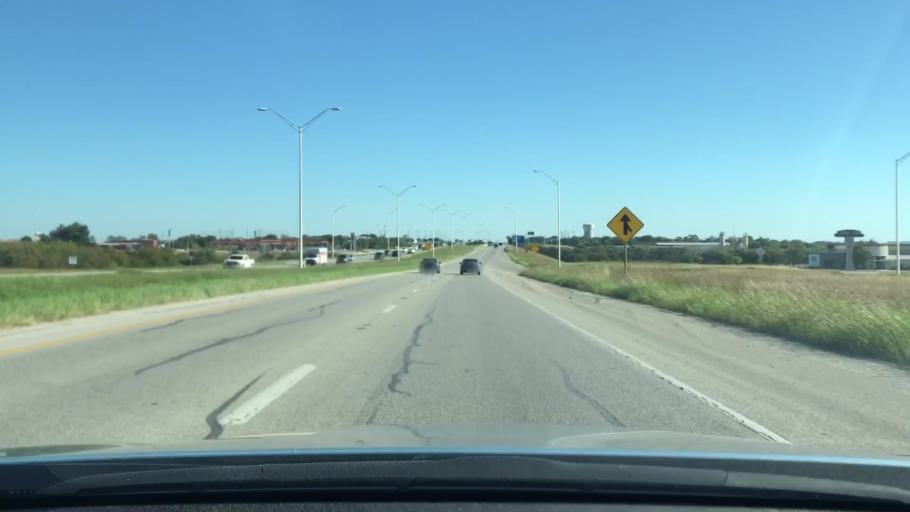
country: US
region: Texas
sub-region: Bexar County
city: Universal City
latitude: 29.5371
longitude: -98.3042
